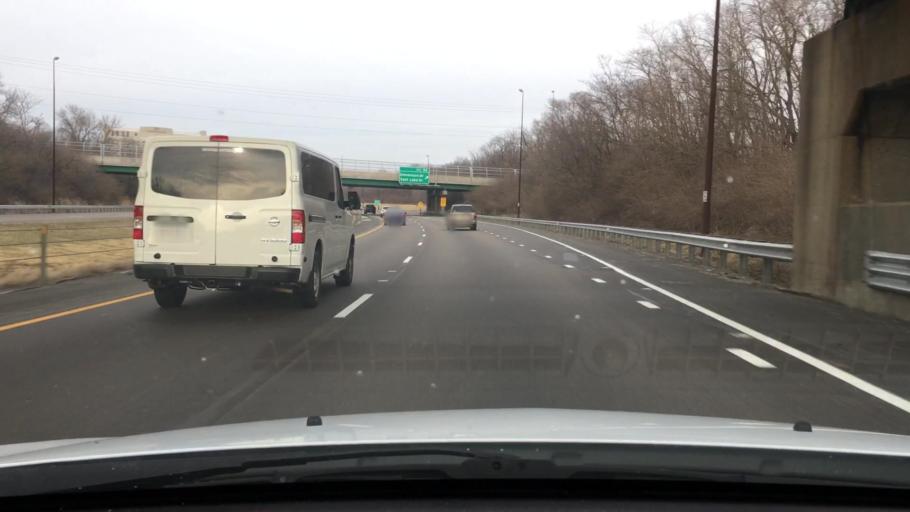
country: US
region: Illinois
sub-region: Sangamon County
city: Southern View
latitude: 39.7570
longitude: -89.6061
